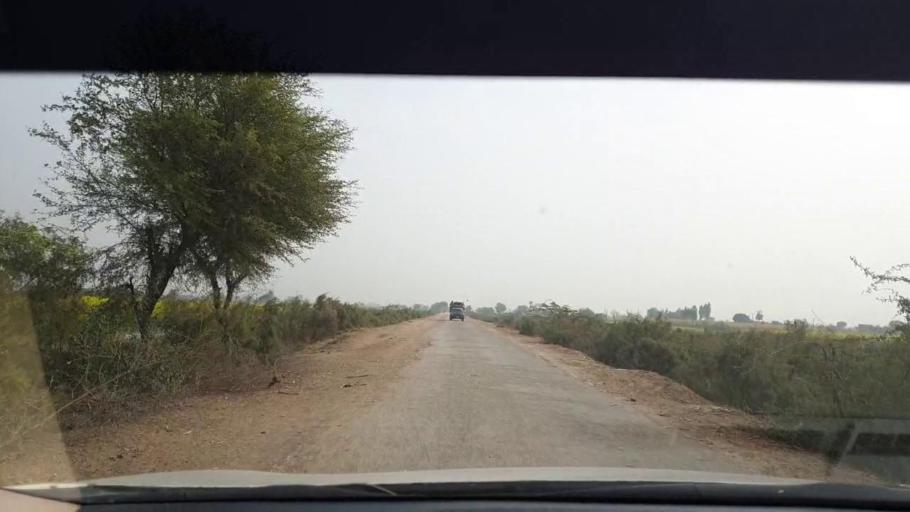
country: PK
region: Sindh
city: Berani
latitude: 25.8470
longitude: 68.8167
